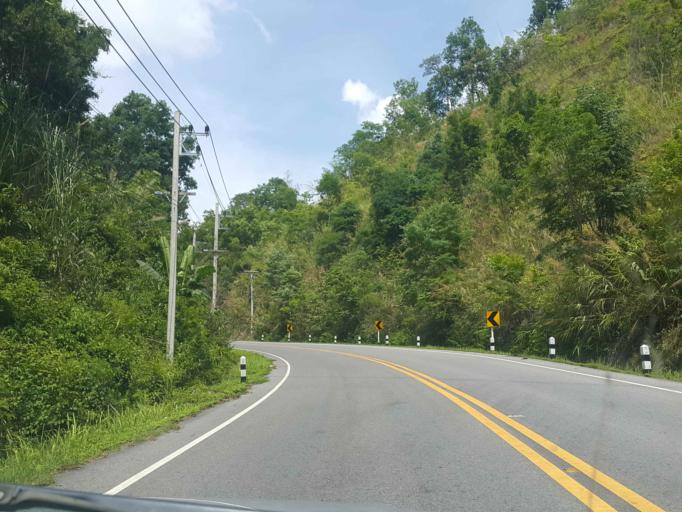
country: TH
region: Nan
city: Ban Luang
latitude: 18.8716
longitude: 100.4810
